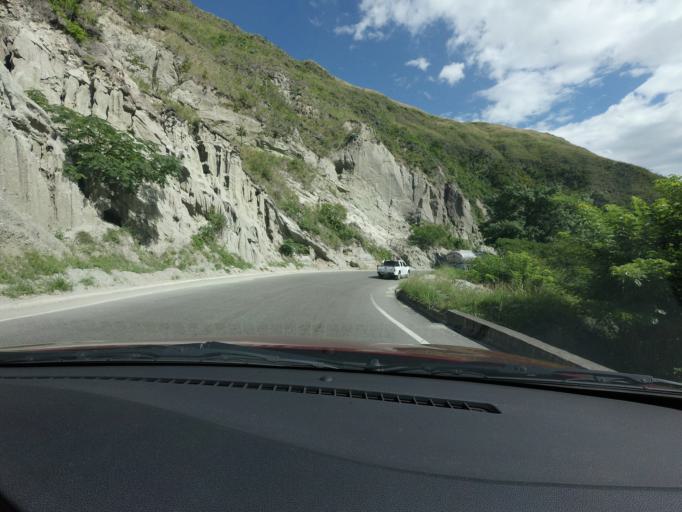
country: CO
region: Huila
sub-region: Gigante
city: Gigante
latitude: 2.4453
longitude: -75.5327
